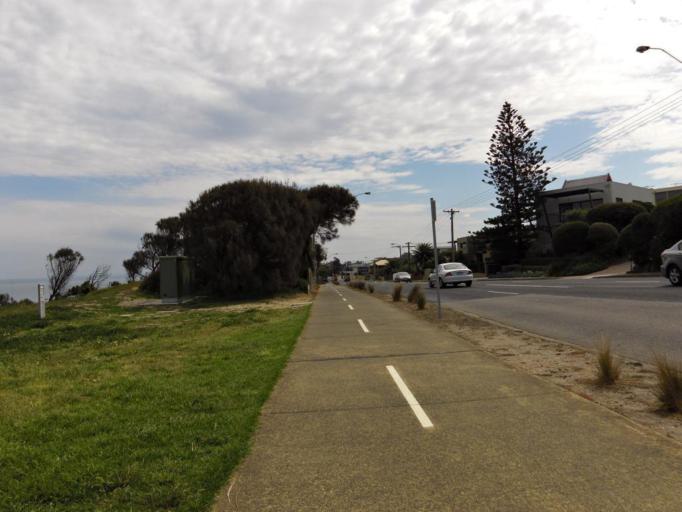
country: AU
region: Victoria
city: Beaumaris
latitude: -37.9845
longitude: 145.0238
